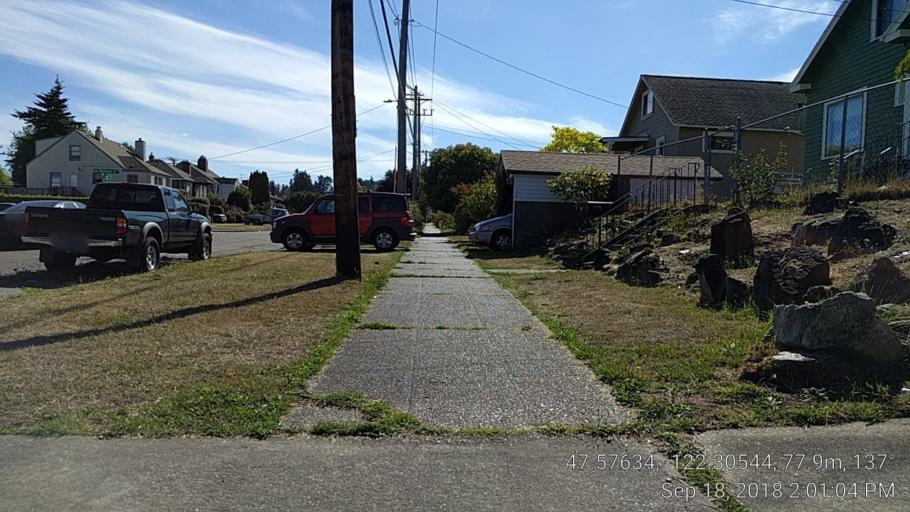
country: US
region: Washington
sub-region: King County
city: Seattle
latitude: 47.5763
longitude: -122.3054
